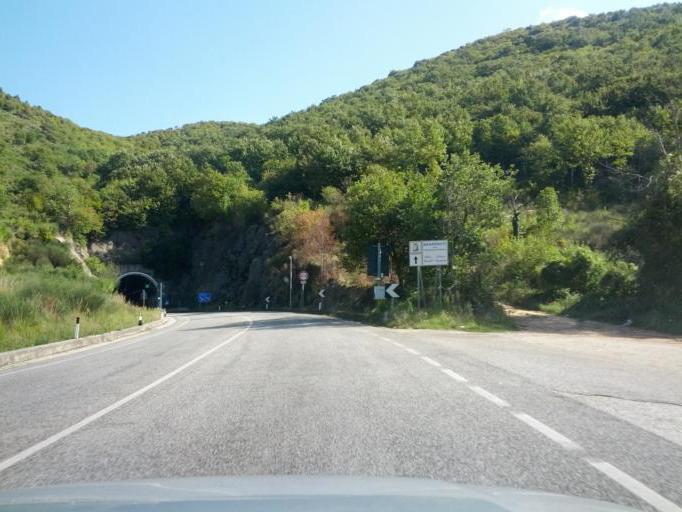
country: IT
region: Campania
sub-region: Provincia di Caserta
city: Mignano Monte Lungo
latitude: 41.4415
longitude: 14.0010
